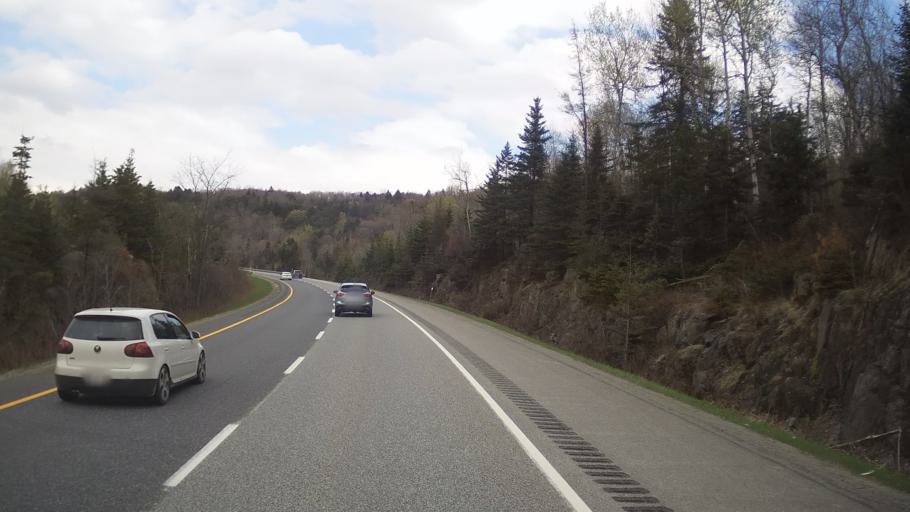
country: CA
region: Quebec
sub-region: Estrie
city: Magog
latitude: 45.2854
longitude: -72.2781
